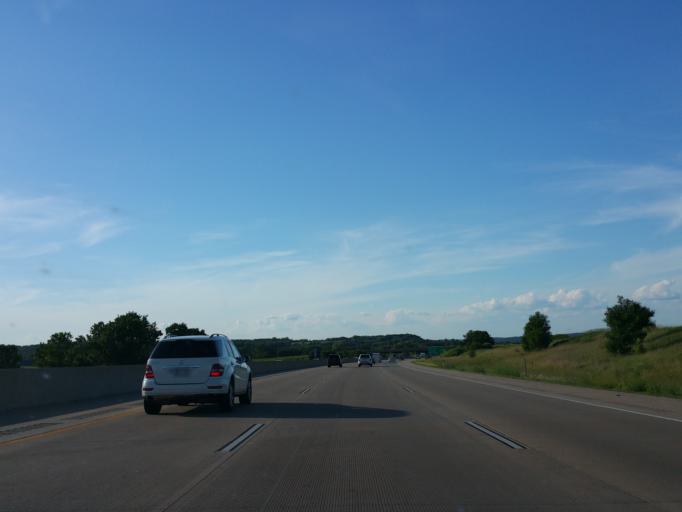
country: US
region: Wisconsin
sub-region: Columbia County
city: Poynette
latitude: 43.3482
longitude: -89.4587
